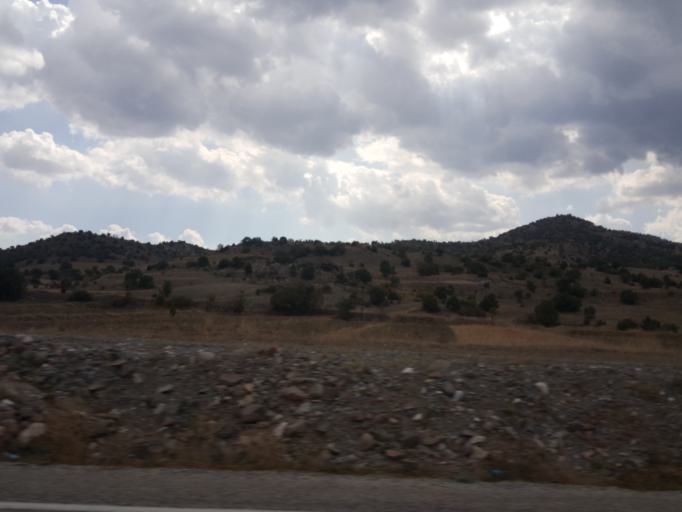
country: TR
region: Yozgat
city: Cekerek
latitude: 40.1919
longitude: 35.4215
